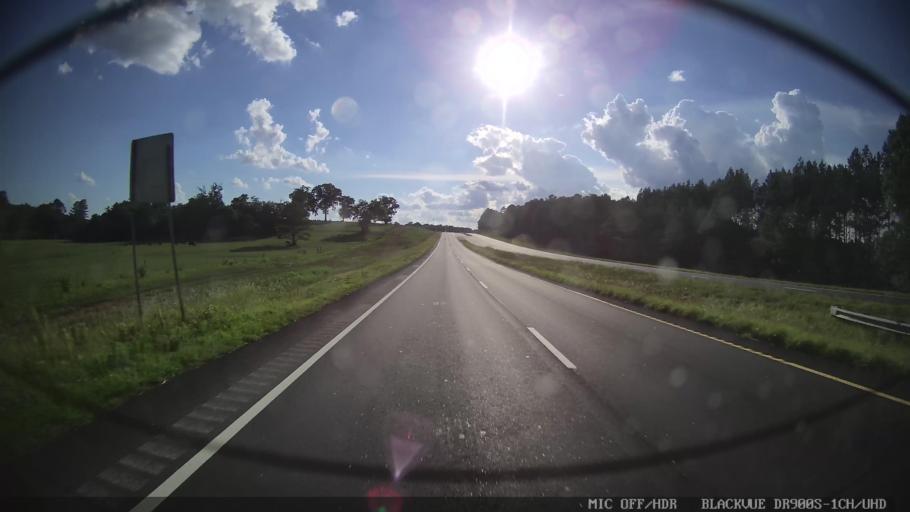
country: US
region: Georgia
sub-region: Floyd County
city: Lindale
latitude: 34.2061
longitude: -85.0762
